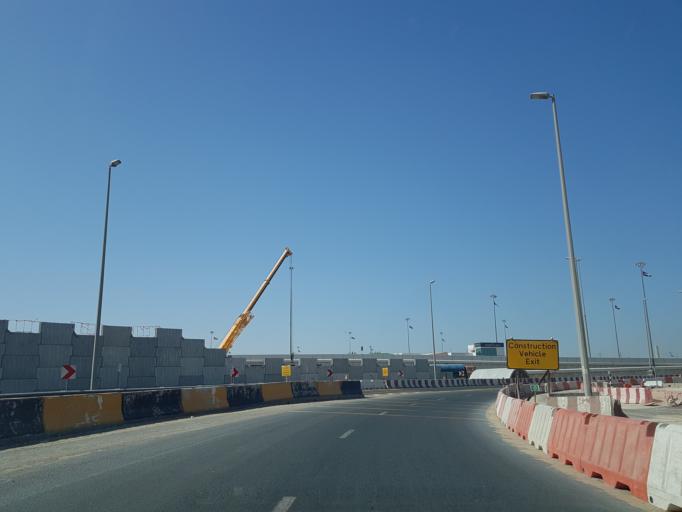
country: AE
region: Dubai
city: Dubai
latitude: 25.0137
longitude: 55.0921
